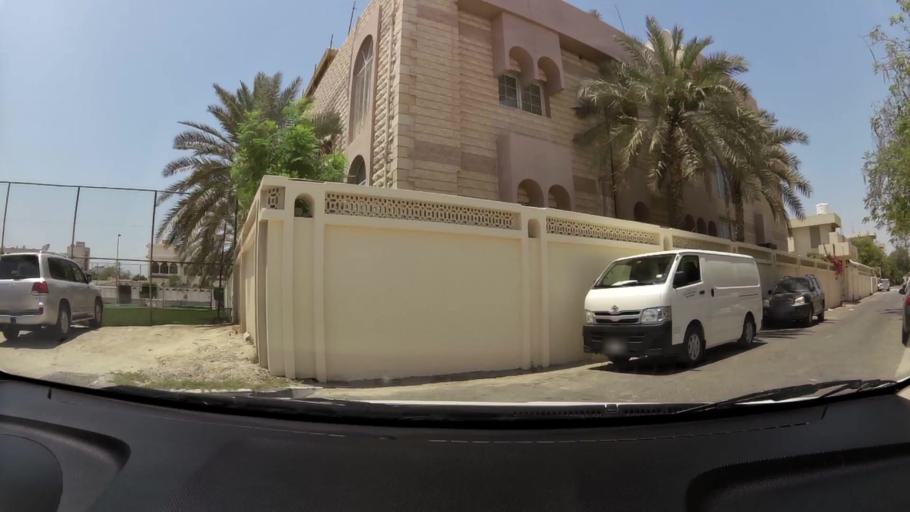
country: AE
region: Ash Shariqah
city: Sharjah
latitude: 25.2917
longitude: 55.3306
